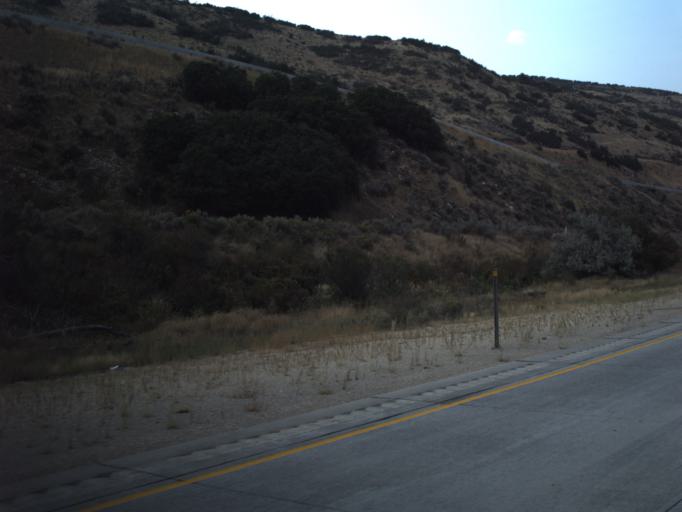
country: US
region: Utah
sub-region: Summit County
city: Snyderville
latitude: 40.7871
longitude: -111.4533
